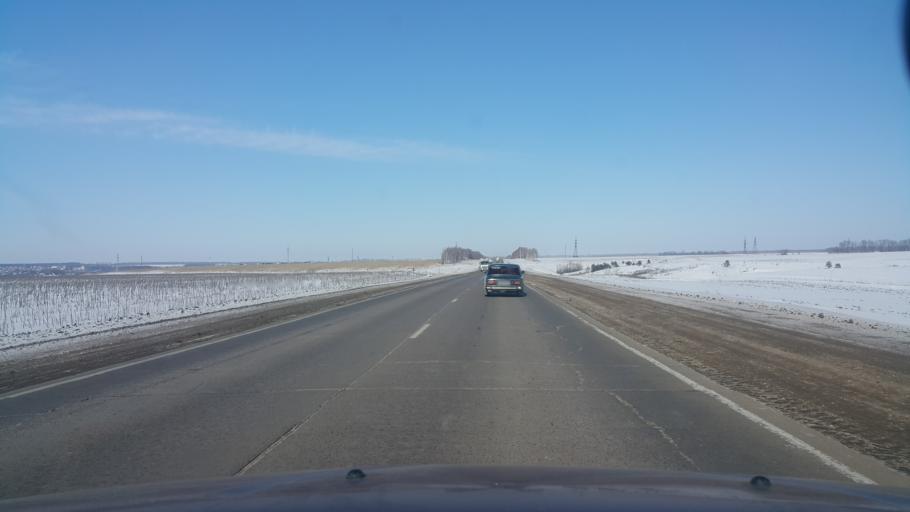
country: RU
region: Tambov
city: Pokrovo-Prigorodnoye
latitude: 52.6286
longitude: 41.3426
